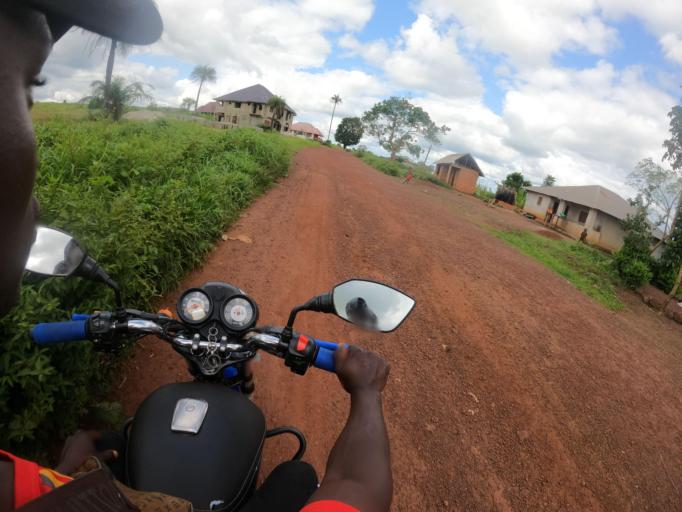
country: SL
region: Northern Province
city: Kamakwie
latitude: 9.5055
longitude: -12.2325
